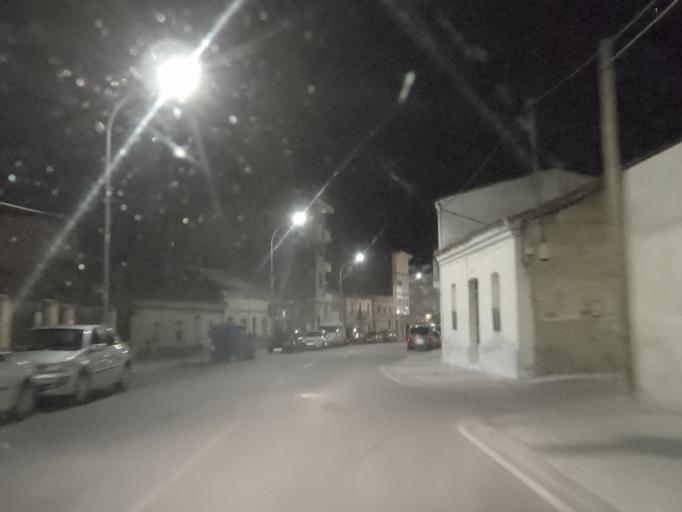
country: ES
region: Castille and Leon
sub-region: Provincia de Zamora
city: Benavente
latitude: 41.9969
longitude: -5.6793
